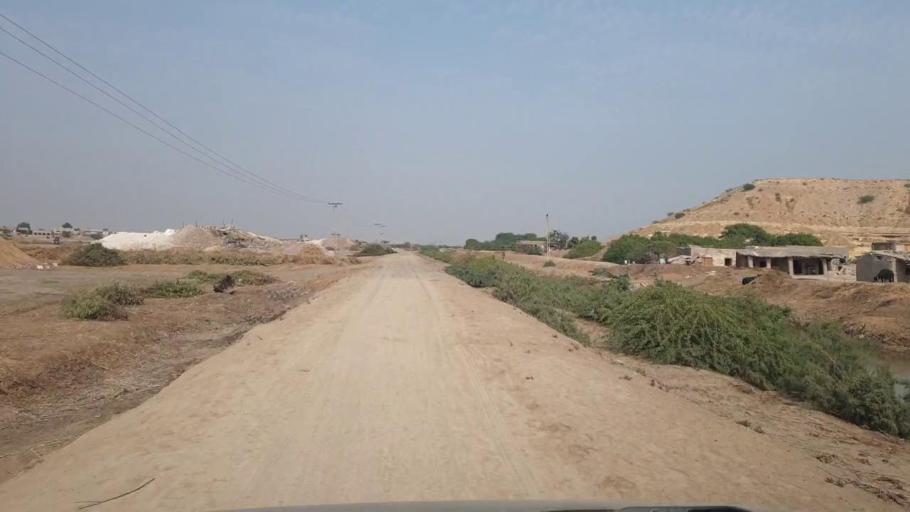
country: PK
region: Sindh
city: Tando Muhammad Khan
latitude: 25.1349
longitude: 68.4567
